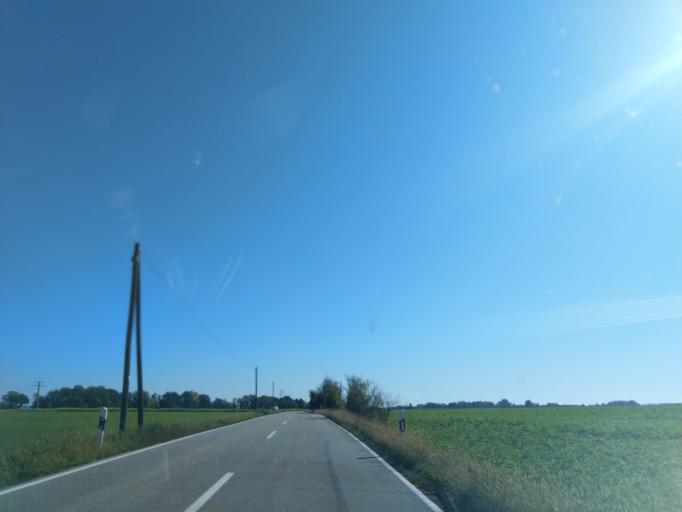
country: DE
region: Bavaria
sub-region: Lower Bavaria
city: Irlbach
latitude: 48.8389
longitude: 12.7589
